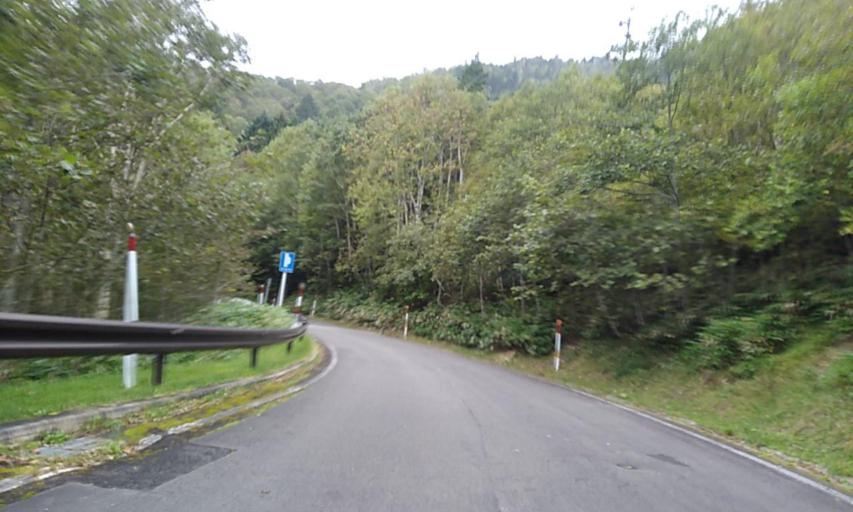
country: JP
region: Hokkaido
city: Bihoro
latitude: 43.5765
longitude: 144.2372
